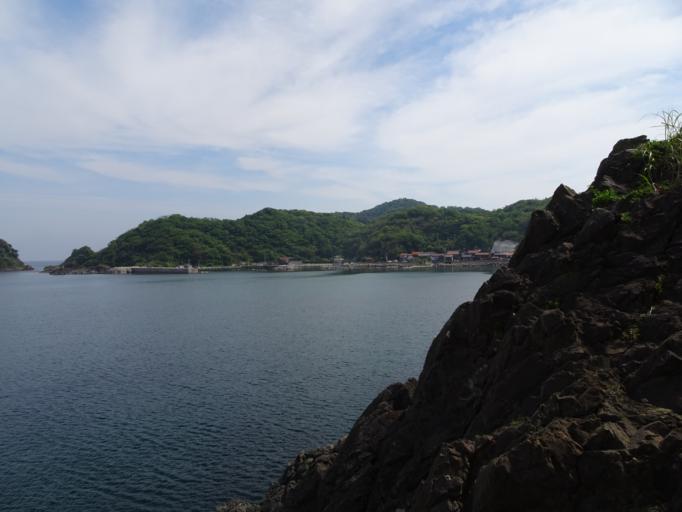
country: JP
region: Shimane
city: Sakaiminato
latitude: 35.5701
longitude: 133.2127
